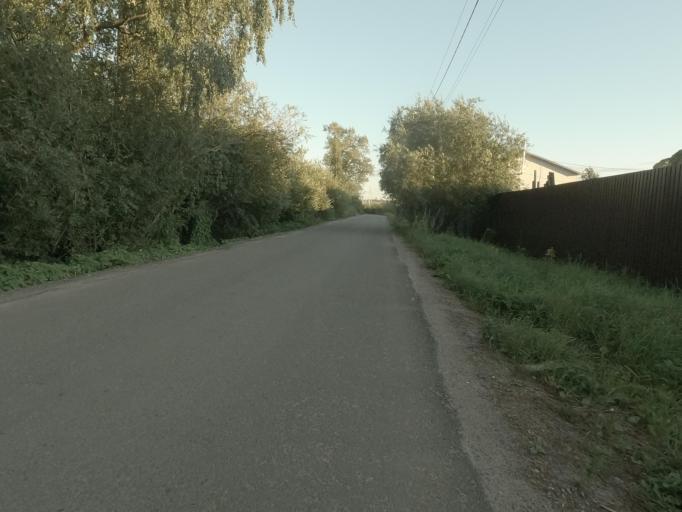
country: RU
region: Leningrad
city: Kirovsk
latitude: 59.8696
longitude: 31.0014
